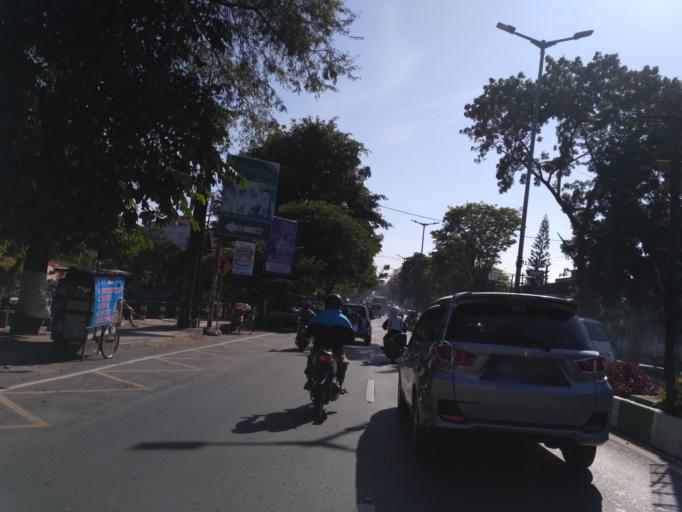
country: ID
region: East Java
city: Malang
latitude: -7.9372
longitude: 112.6444
